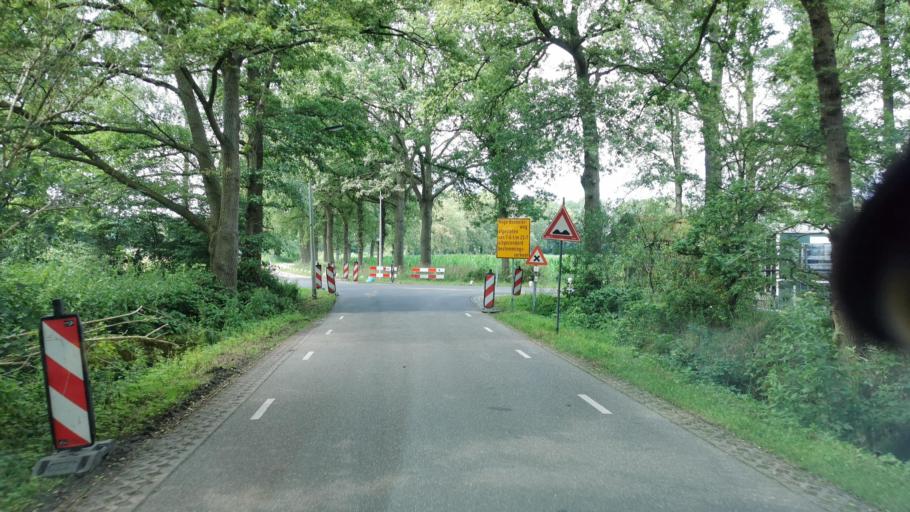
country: NL
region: Overijssel
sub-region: Gemeente Losser
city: Losser
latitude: 52.2354
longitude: 6.9536
